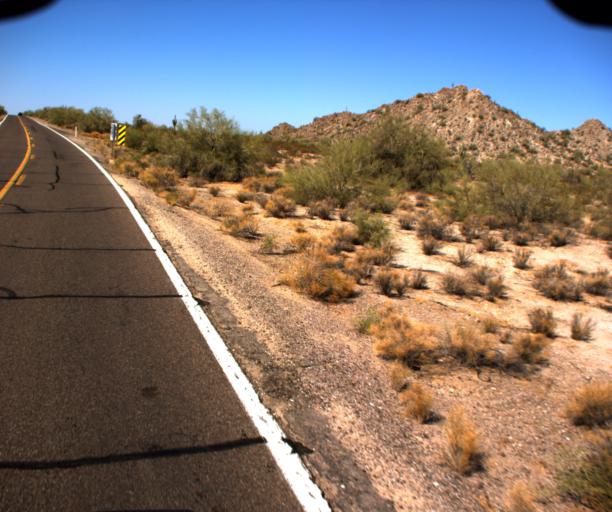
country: US
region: Arizona
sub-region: Pinal County
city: Sacaton
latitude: 33.0393
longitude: -111.7291
